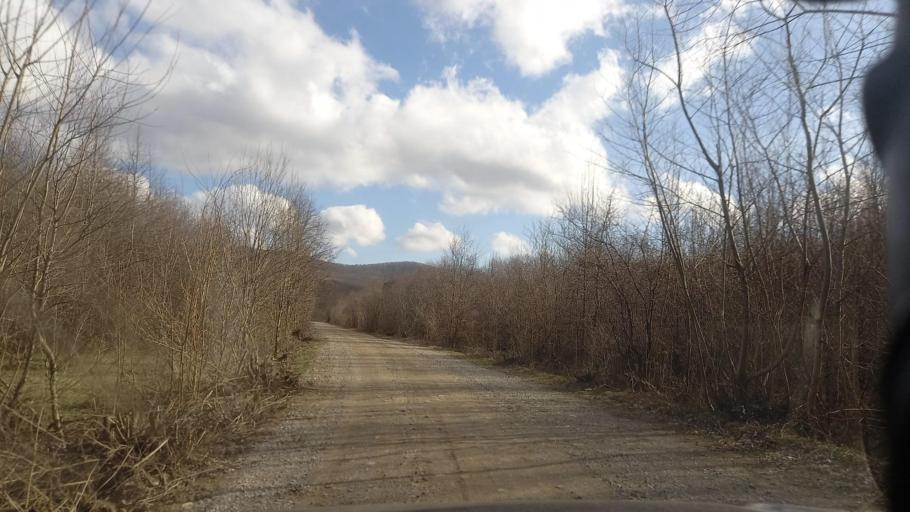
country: RU
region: Krasnodarskiy
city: Smolenskaya
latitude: 44.6178
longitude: 38.8270
